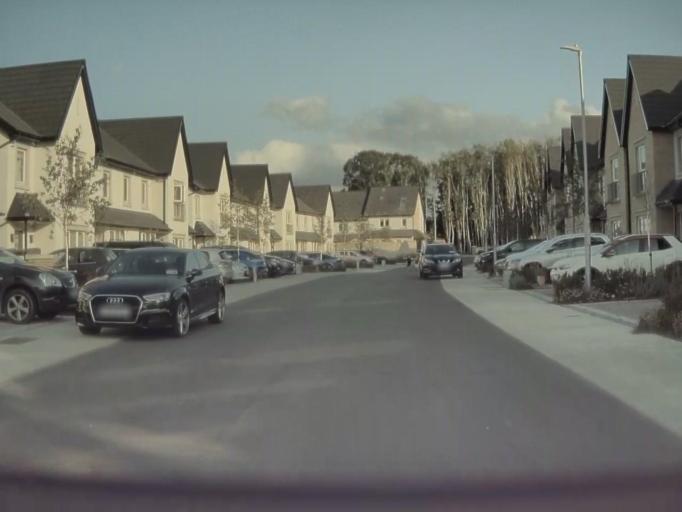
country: IE
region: Leinster
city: Foxrock
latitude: 53.2415
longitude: -6.2024
